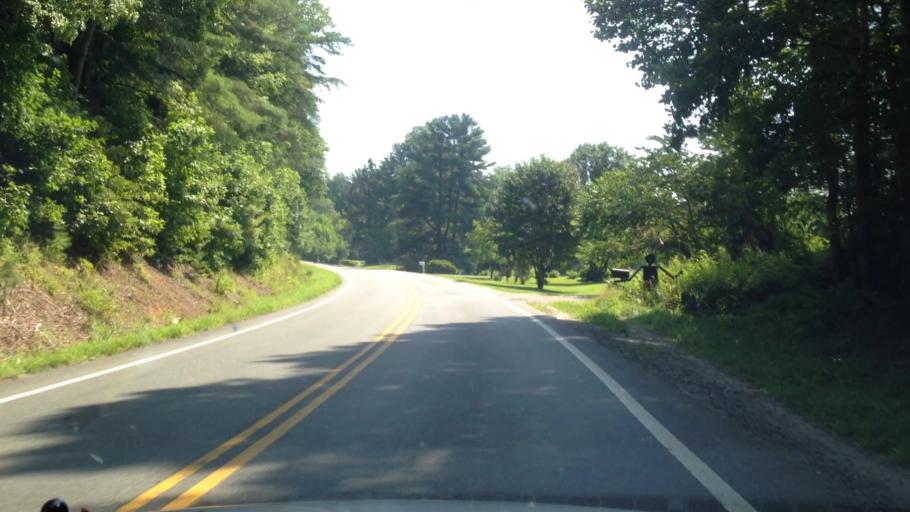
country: US
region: Virginia
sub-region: Patrick County
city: Stuart
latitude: 36.5770
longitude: -80.3740
